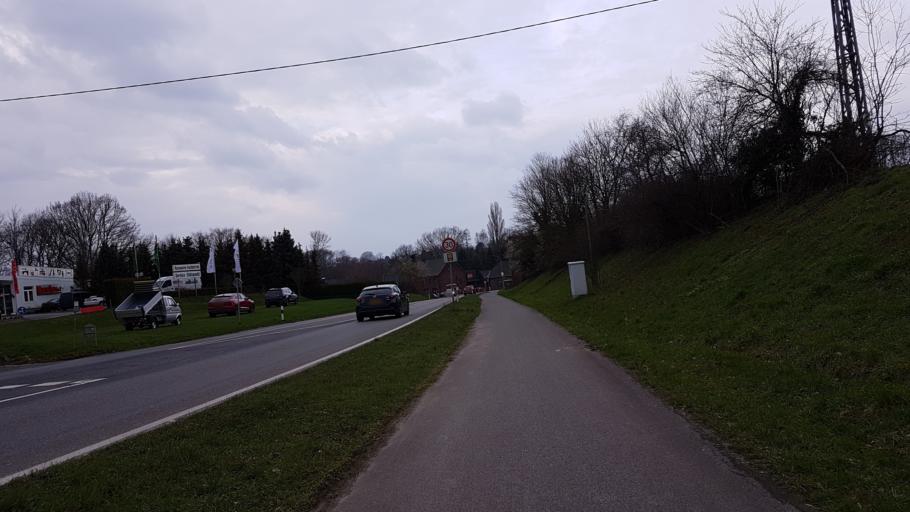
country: DE
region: North Rhine-Westphalia
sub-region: Regierungsbezirk Dusseldorf
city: Bruggen
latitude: 51.2111
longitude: 6.1771
